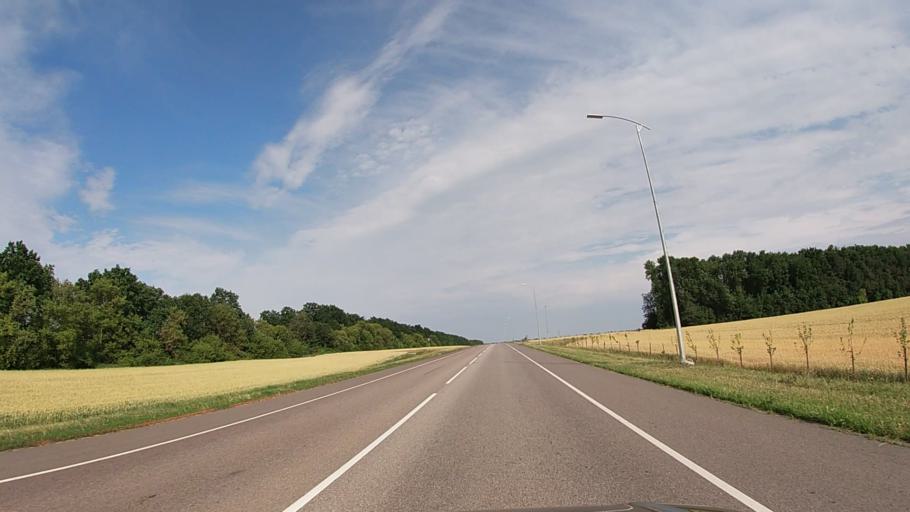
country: RU
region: Belgorod
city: Proletarskiy
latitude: 50.8243
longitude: 35.7838
